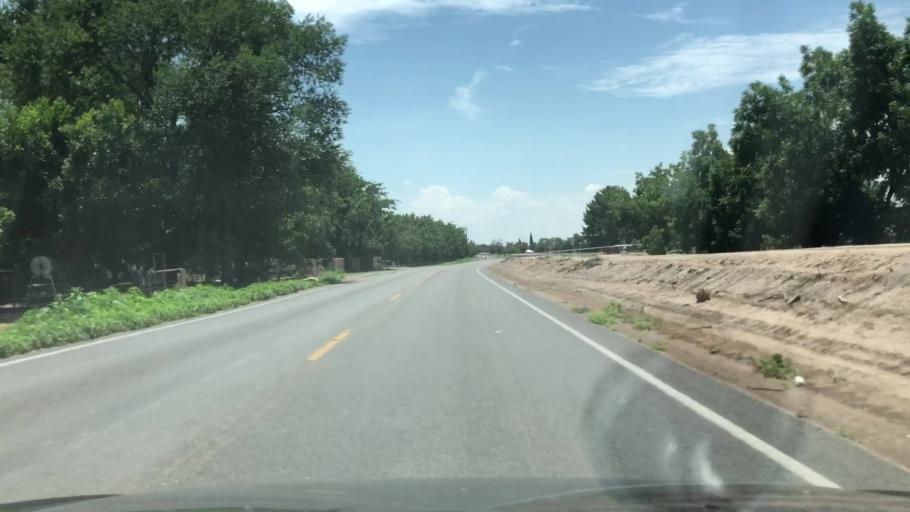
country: US
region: New Mexico
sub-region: Dona Ana County
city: Anthony
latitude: 32.0156
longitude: -106.6676
